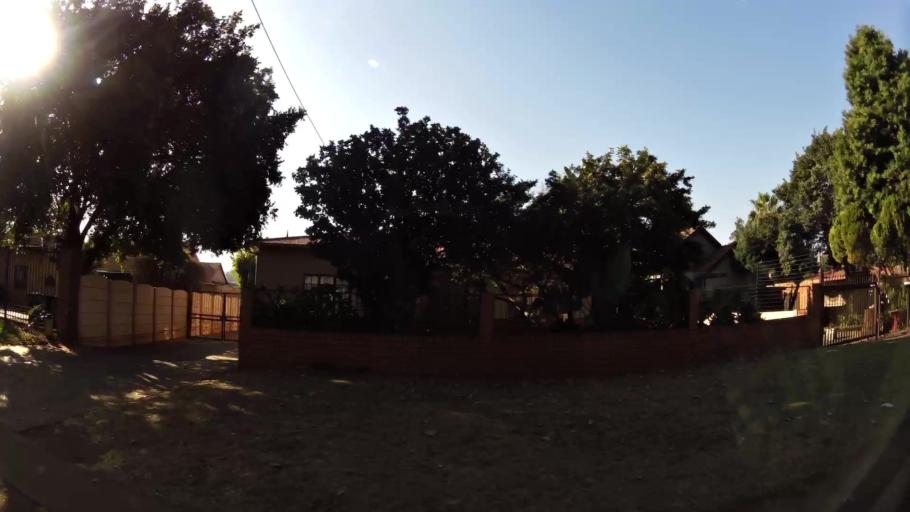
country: ZA
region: Gauteng
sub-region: City of Tshwane Metropolitan Municipality
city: Pretoria
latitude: -25.7150
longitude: 28.1501
